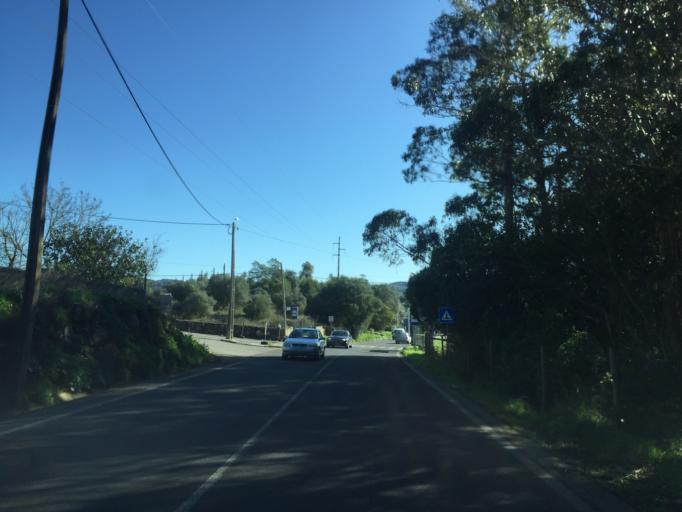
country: PT
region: Lisbon
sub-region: Sintra
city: Pero Pinheiro
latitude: 38.8407
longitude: -9.3154
